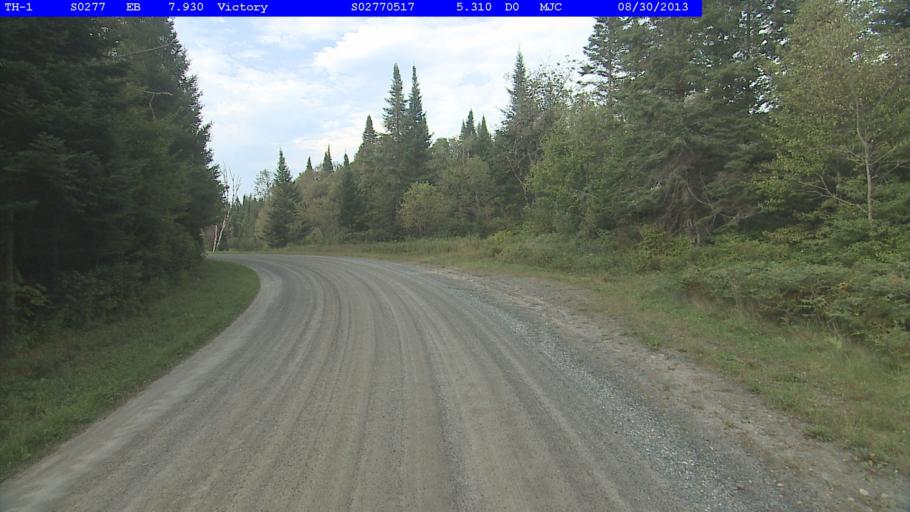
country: US
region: Vermont
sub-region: Caledonia County
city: Lyndonville
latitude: 44.5454
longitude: -71.7847
